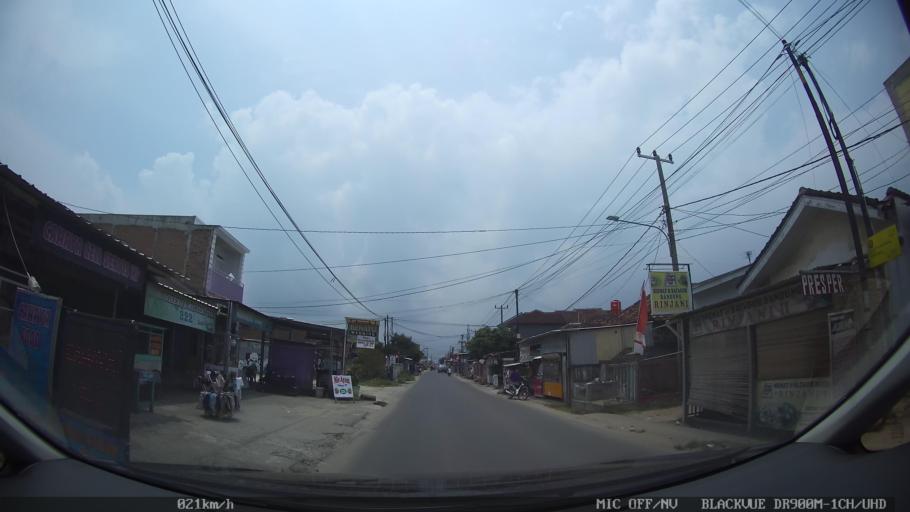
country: ID
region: Lampung
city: Kedaton
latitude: -5.3912
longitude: 105.2962
